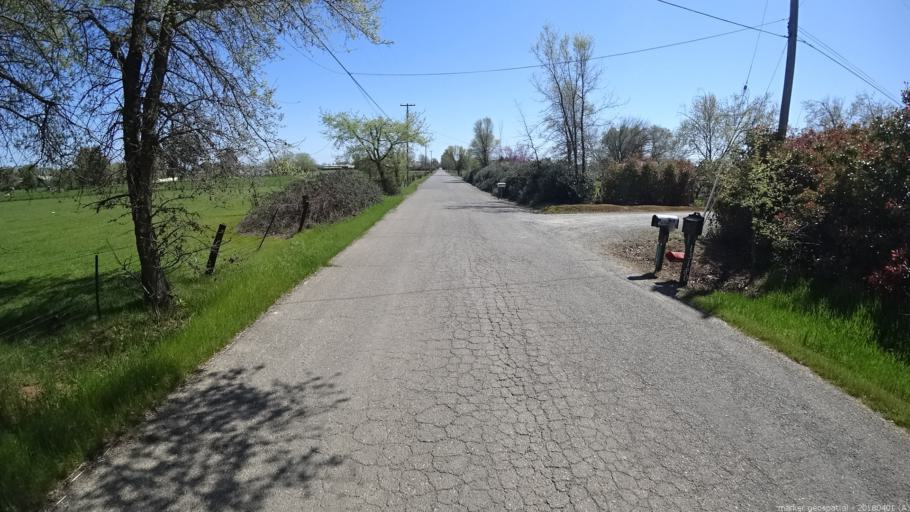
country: US
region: California
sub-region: Sacramento County
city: Rancho Murieta
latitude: 38.4519
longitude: -121.1730
